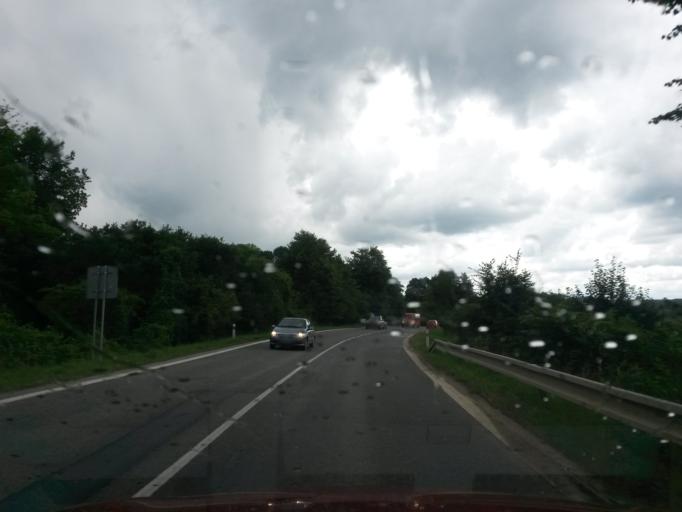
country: SK
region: Kosicky
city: Strazske
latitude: 48.8632
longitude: 21.7687
